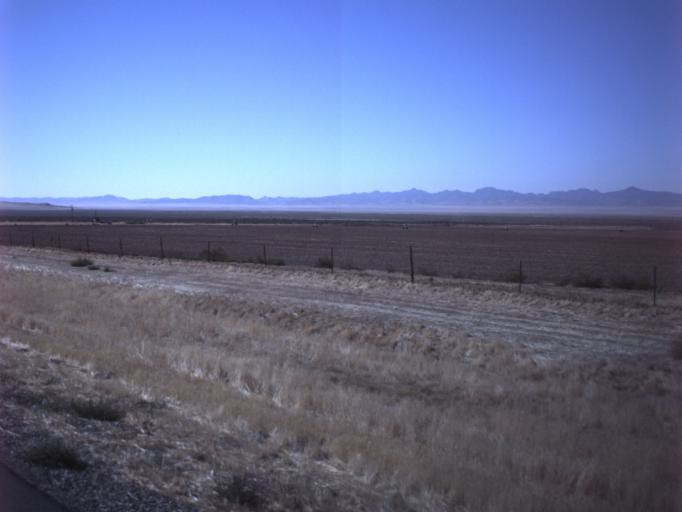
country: US
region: Utah
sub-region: Tooele County
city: Grantsville
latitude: 40.5001
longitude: -112.7480
